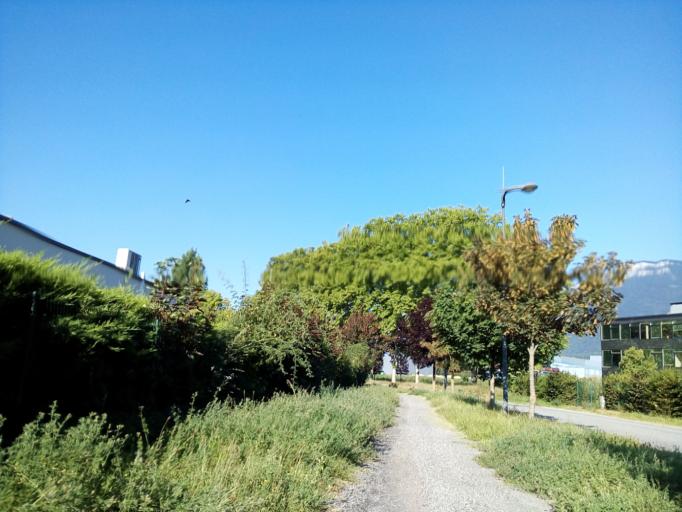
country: FR
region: Rhone-Alpes
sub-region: Departement de l'Isere
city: Crolles
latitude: 45.2682
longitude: 5.8883
